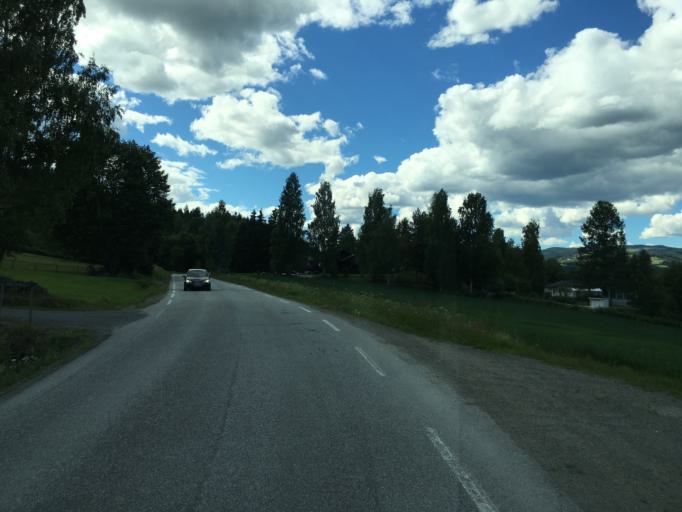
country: NO
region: Oppland
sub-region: Nordre Land
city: Dokka
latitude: 60.8125
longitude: 10.1006
